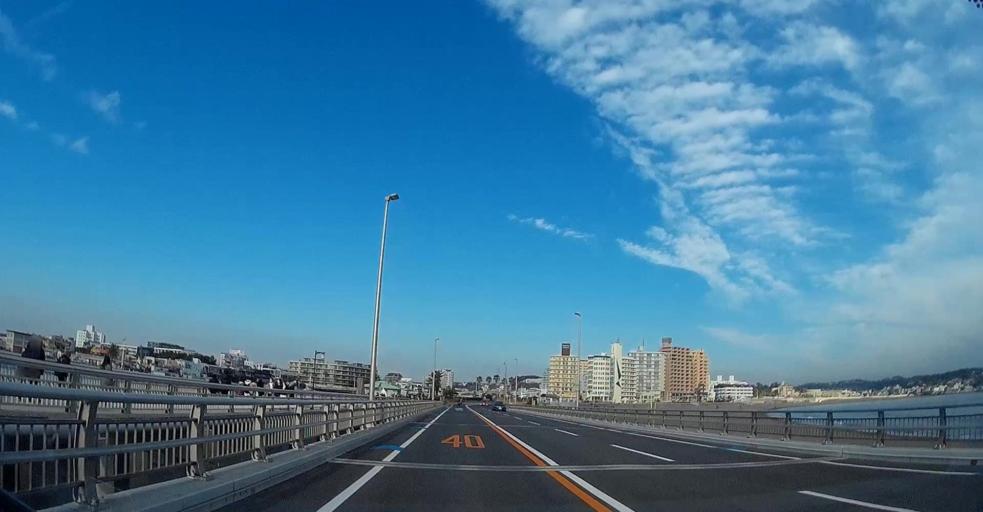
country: JP
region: Kanagawa
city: Fujisawa
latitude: 35.3032
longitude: 139.4806
